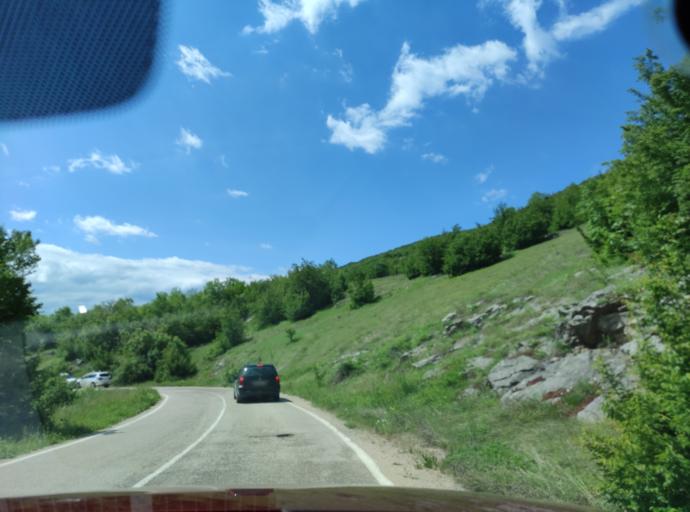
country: BG
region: Montana
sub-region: Obshtina Chiprovtsi
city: Chiprovtsi
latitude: 43.4923
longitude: 22.8036
